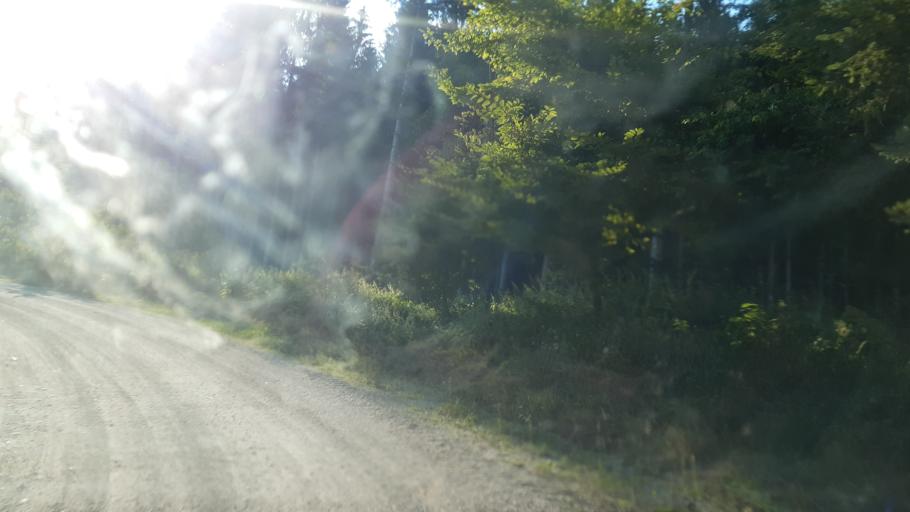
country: SI
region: Dolenjske Toplice
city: Dolenjske Toplice
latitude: 45.7168
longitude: 15.0167
